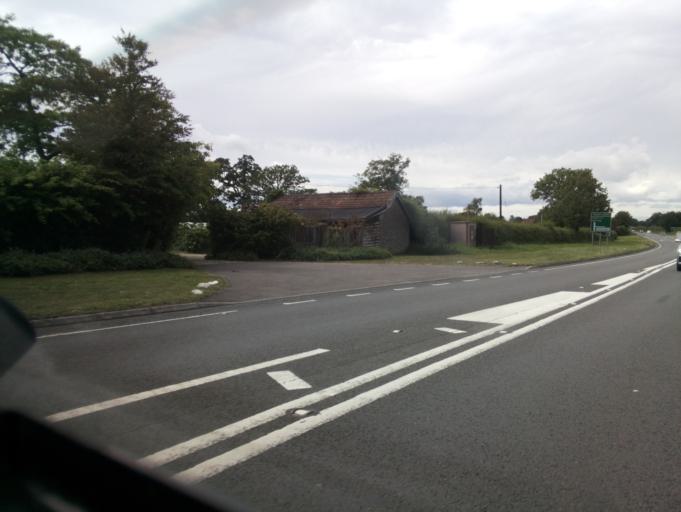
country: GB
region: England
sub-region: Somerset
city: Yeovil
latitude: 50.8714
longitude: -2.5965
